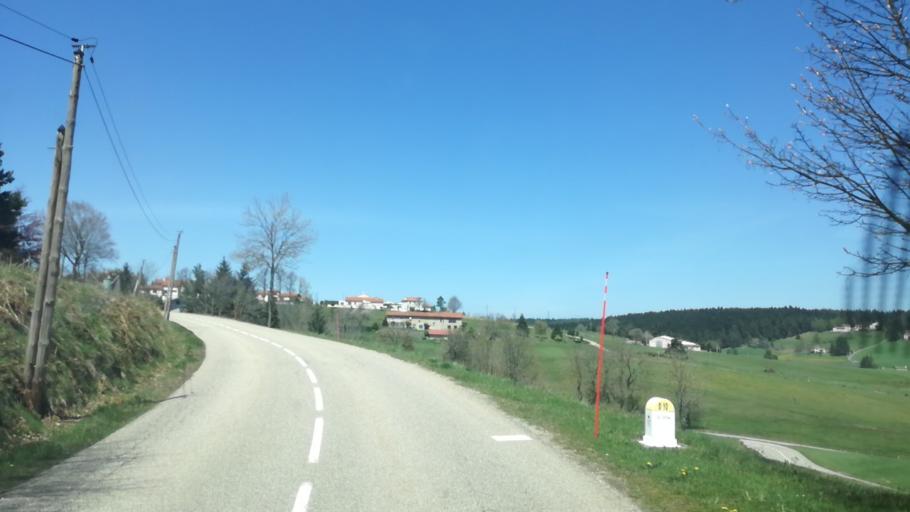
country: FR
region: Rhone-Alpes
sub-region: Departement de la Loire
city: Jonzieux
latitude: 45.3094
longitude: 4.3674
